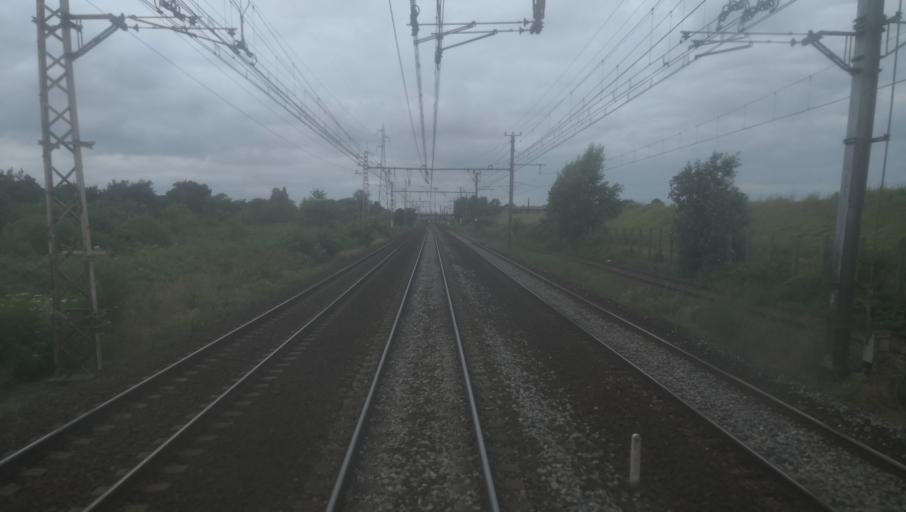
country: FR
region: Midi-Pyrenees
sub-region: Departement de la Haute-Garonne
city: Fenouillet
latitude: 43.6801
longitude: 1.4039
